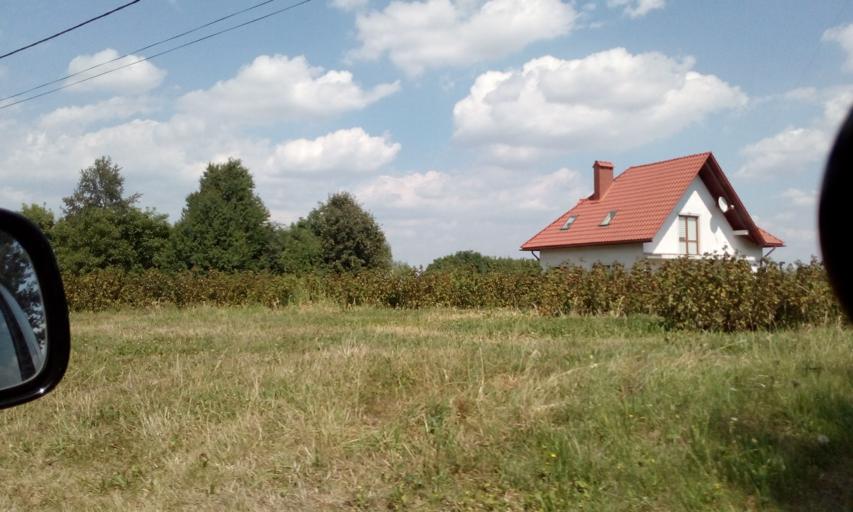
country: PL
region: Subcarpathian Voivodeship
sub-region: Powiat lancucki
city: Wysoka
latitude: 50.0482
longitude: 22.2406
